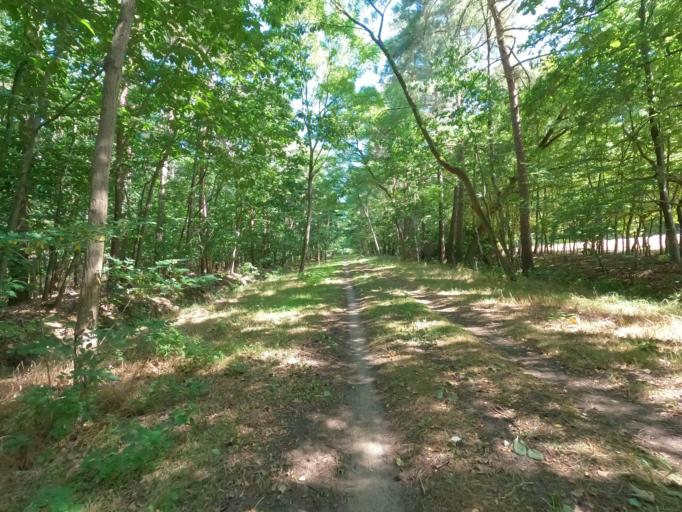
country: BE
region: Flanders
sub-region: Provincie Antwerpen
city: Vorselaar
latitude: 51.2120
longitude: 4.7965
